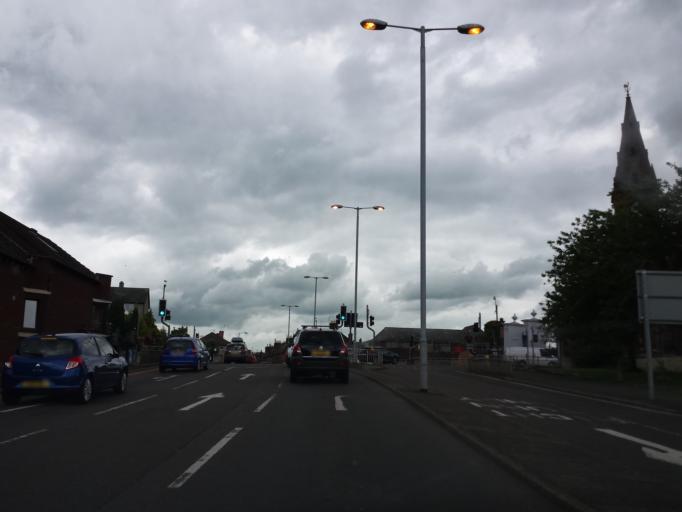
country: GB
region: Scotland
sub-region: Dumfries and Galloway
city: Dumfries
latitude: 55.0650
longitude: -3.6080
